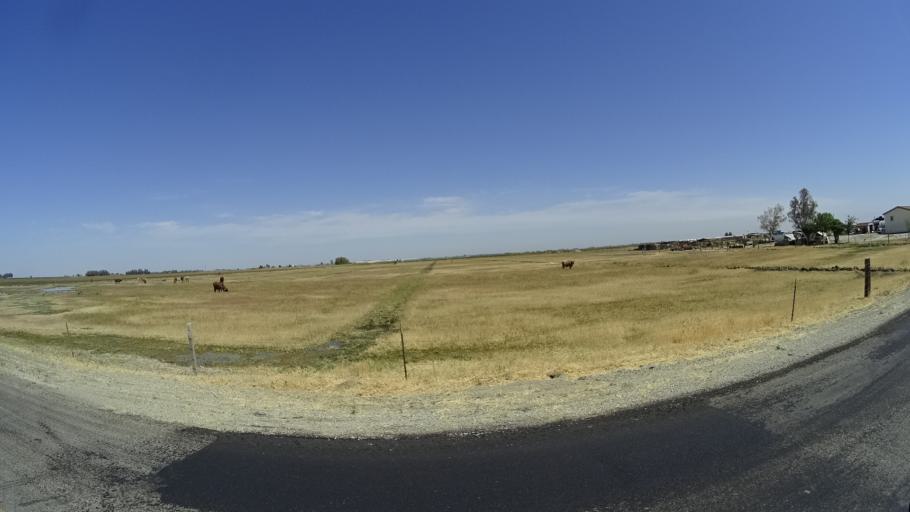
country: US
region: California
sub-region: Kings County
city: Stratford
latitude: 36.1892
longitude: -119.7568
